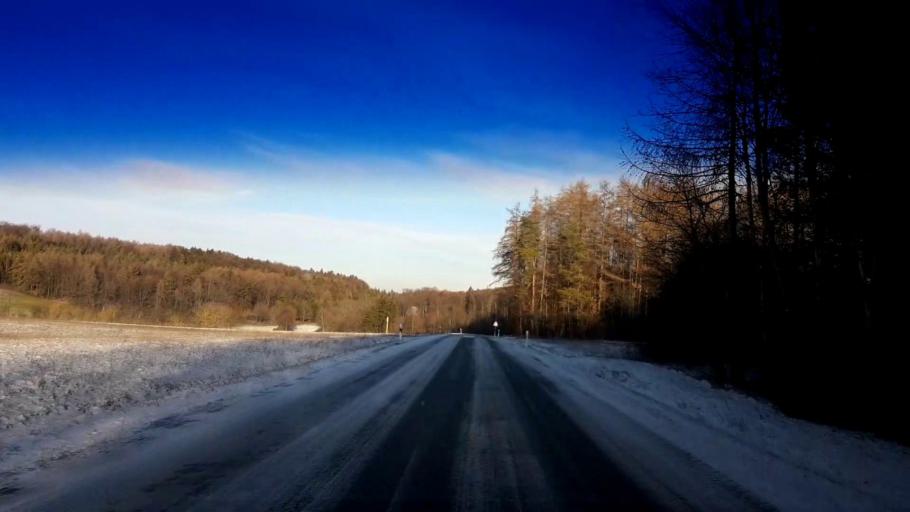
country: DE
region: Bavaria
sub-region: Upper Franconia
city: Heiligenstadt
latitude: 49.8497
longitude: 11.1417
